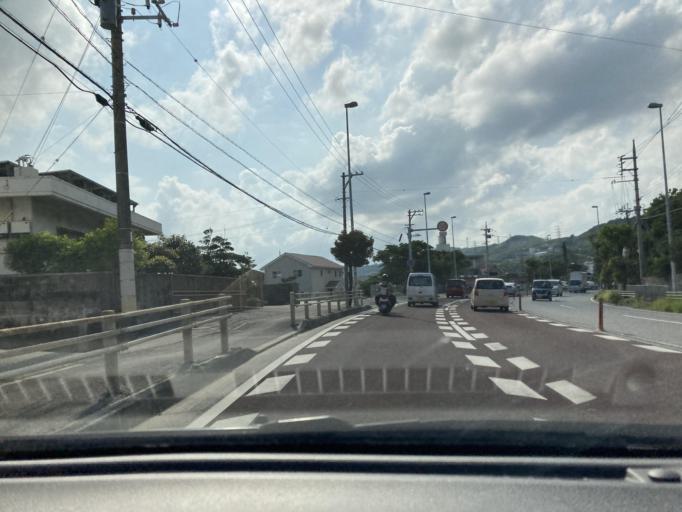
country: JP
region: Okinawa
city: Ginowan
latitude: 26.2773
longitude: 127.8077
